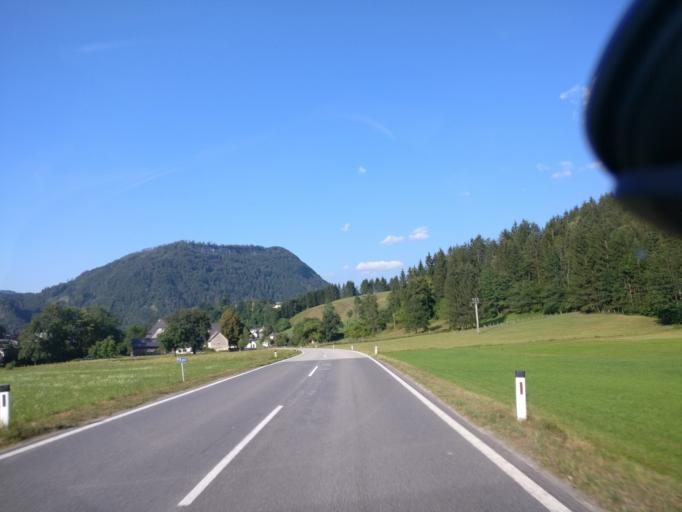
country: AT
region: Lower Austria
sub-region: Politischer Bezirk Scheibbs
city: Gostling an der Ybbs
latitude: 47.7983
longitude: 14.9257
